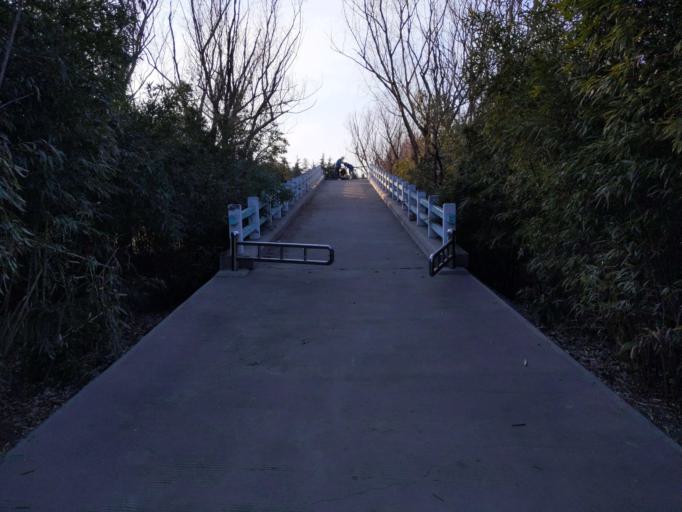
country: CN
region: Henan Sheng
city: Puyang
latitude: 35.7798
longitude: 114.9527
